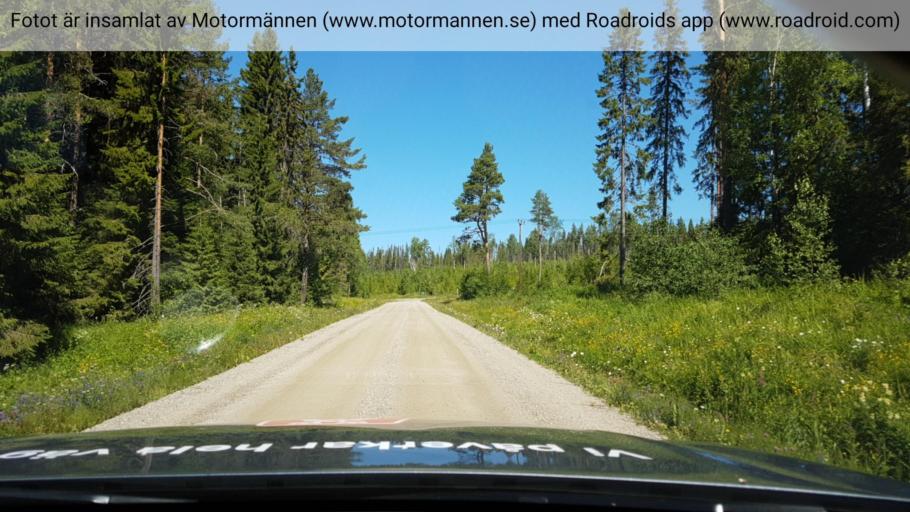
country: SE
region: Jaemtland
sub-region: Braecke Kommun
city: Braecke
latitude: 62.8234
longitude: 15.2215
